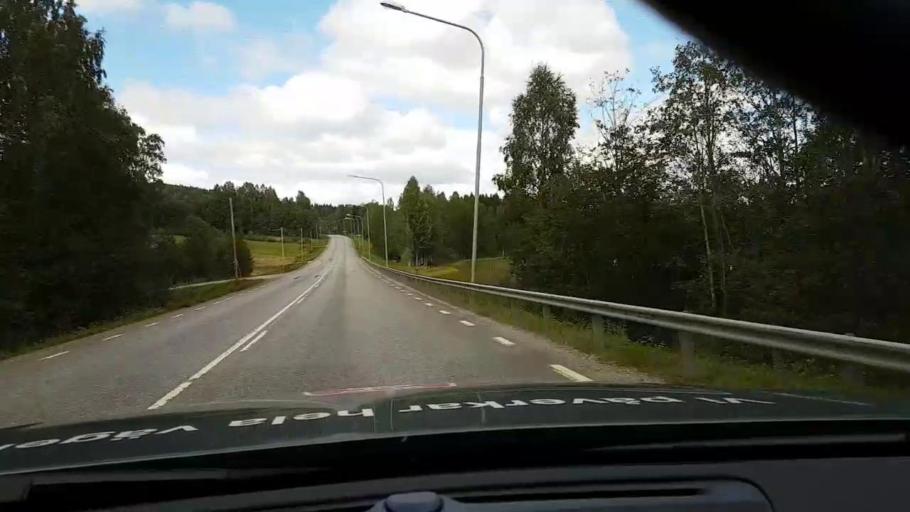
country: SE
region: Vaesternorrland
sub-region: OErnskoeldsviks Kommun
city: Bredbyn
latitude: 63.4860
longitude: 18.0862
